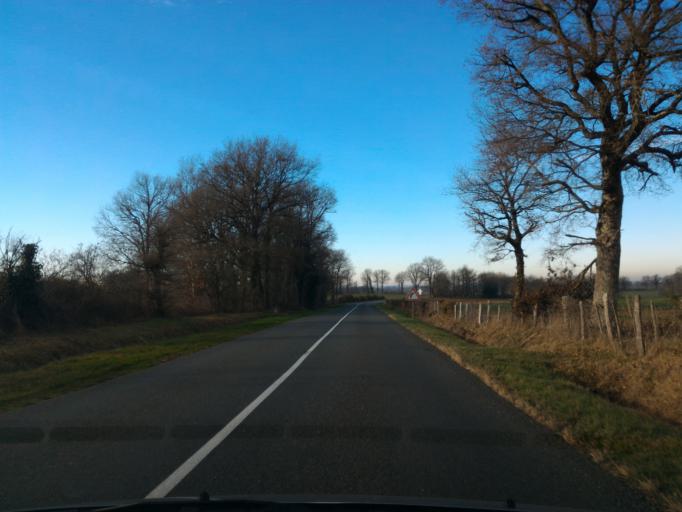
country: FR
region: Poitou-Charentes
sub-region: Departement de la Charente
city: Confolens
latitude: 46.0311
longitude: 0.5722
